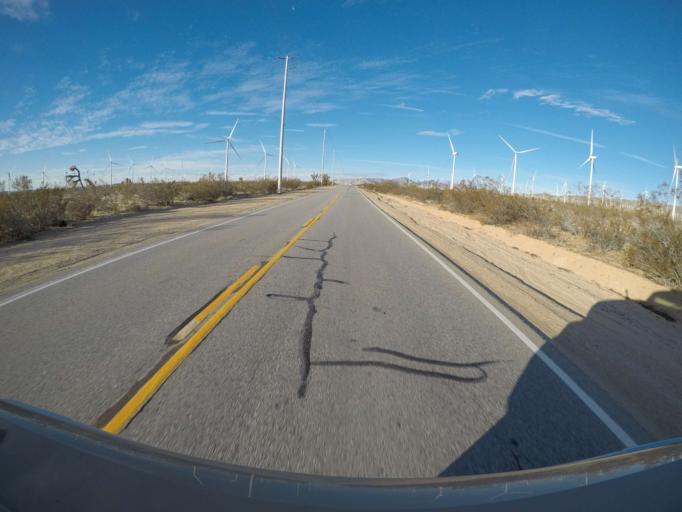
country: US
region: California
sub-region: Kern County
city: Mojave
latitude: 35.0458
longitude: -118.2197
